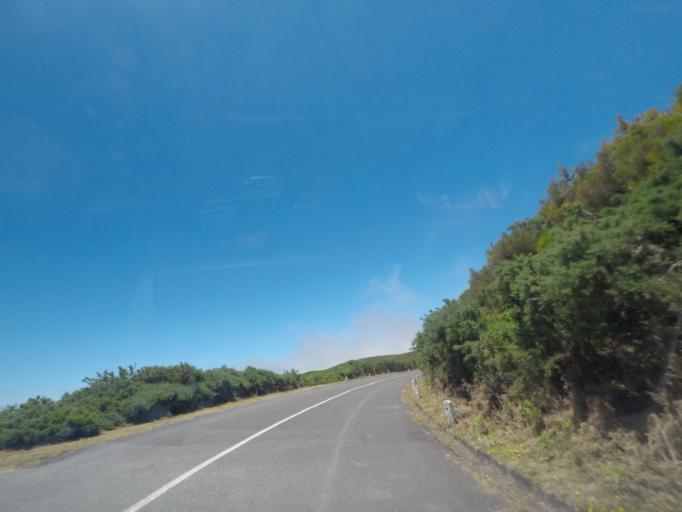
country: PT
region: Madeira
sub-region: Calheta
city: Faja da Ovelha
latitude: 32.8020
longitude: -17.1914
